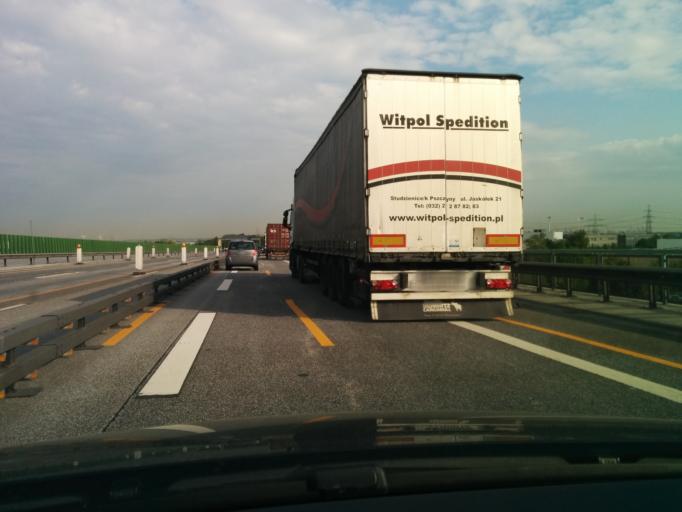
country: DE
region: Hamburg
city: Harburg
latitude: 53.4707
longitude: 9.9208
